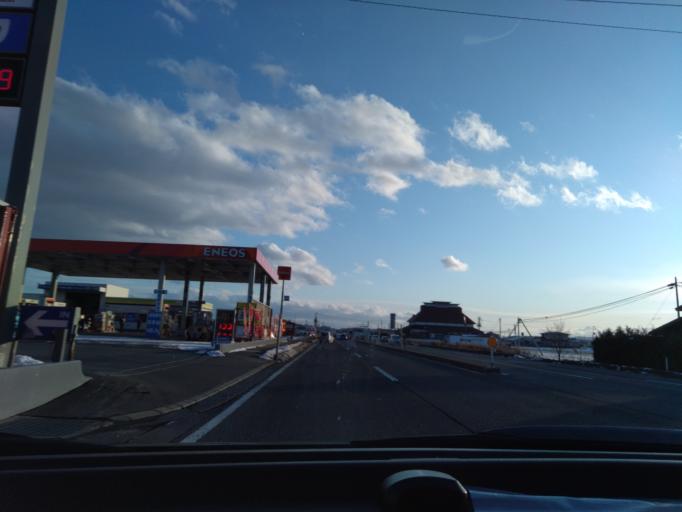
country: JP
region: Iwate
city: Morioka-shi
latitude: 39.5937
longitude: 141.1707
